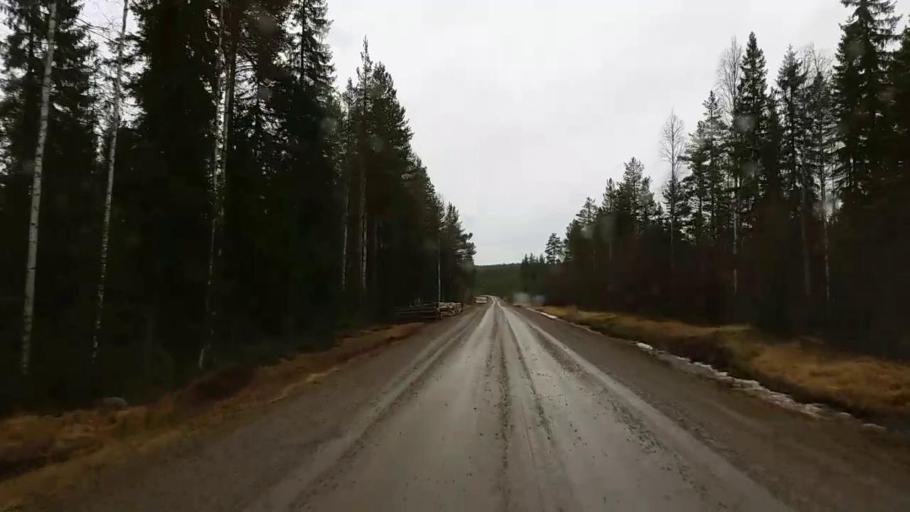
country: SE
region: Gaevleborg
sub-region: Ljusdals Kommun
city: Farila
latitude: 62.1180
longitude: 15.6847
